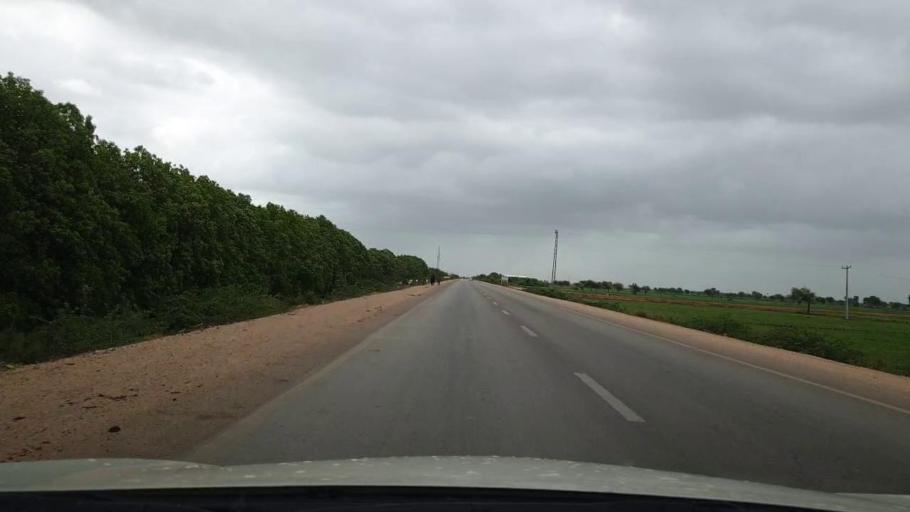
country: PK
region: Sindh
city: Badin
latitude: 24.6552
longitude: 68.7350
